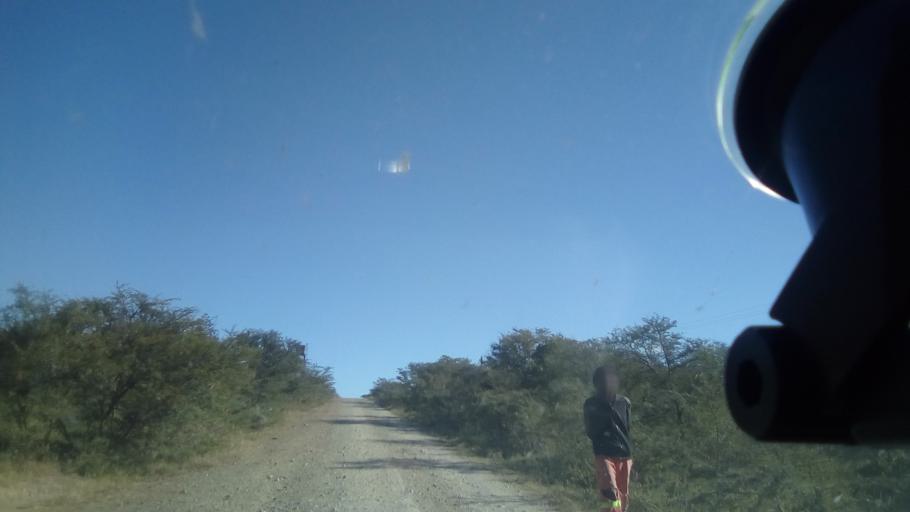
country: ZA
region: Eastern Cape
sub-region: Buffalo City Metropolitan Municipality
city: Bhisho
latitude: -32.7543
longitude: 27.3368
